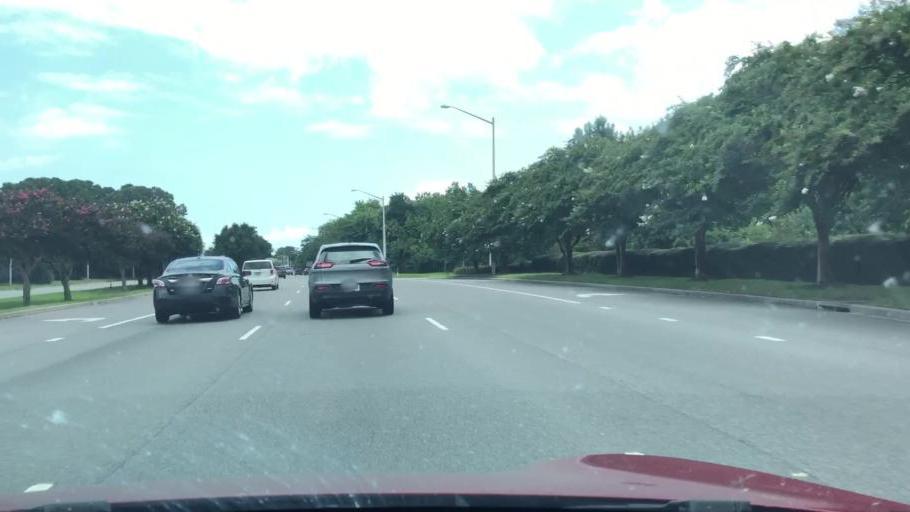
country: US
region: Virginia
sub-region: City of Chesapeake
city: Chesapeake
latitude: 36.8569
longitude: -76.1340
